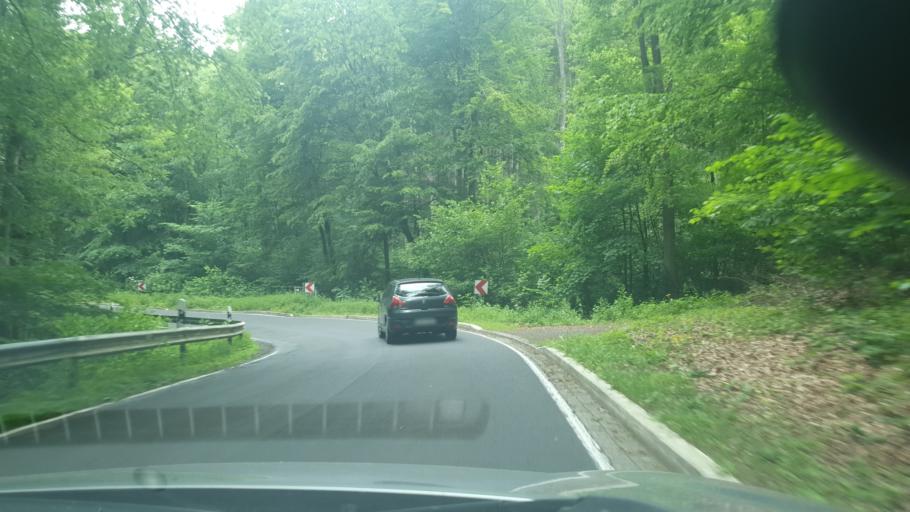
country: DE
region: Rheinland-Pfalz
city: Neuhausel
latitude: 50.3994
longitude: 7.7188
